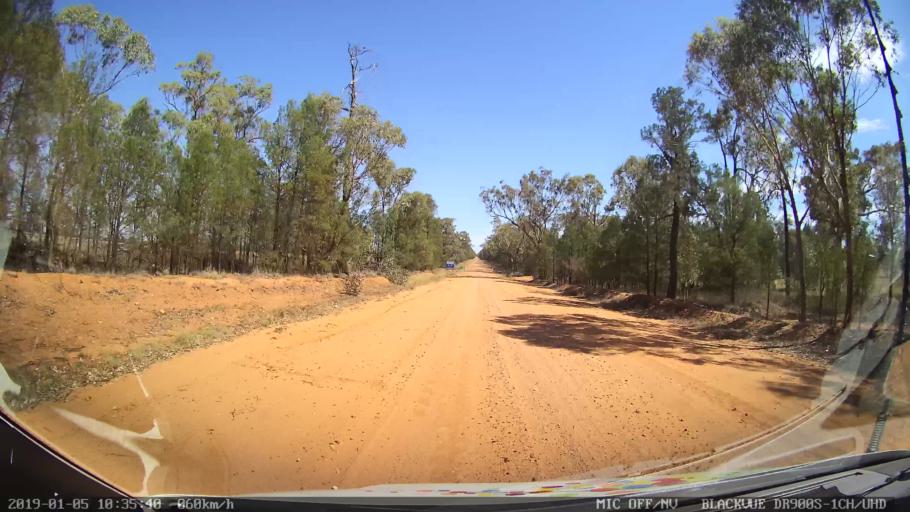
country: AU
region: New South Wales
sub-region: Gilgandra
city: Gilgandra
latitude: -31.4884
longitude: 148.9281
